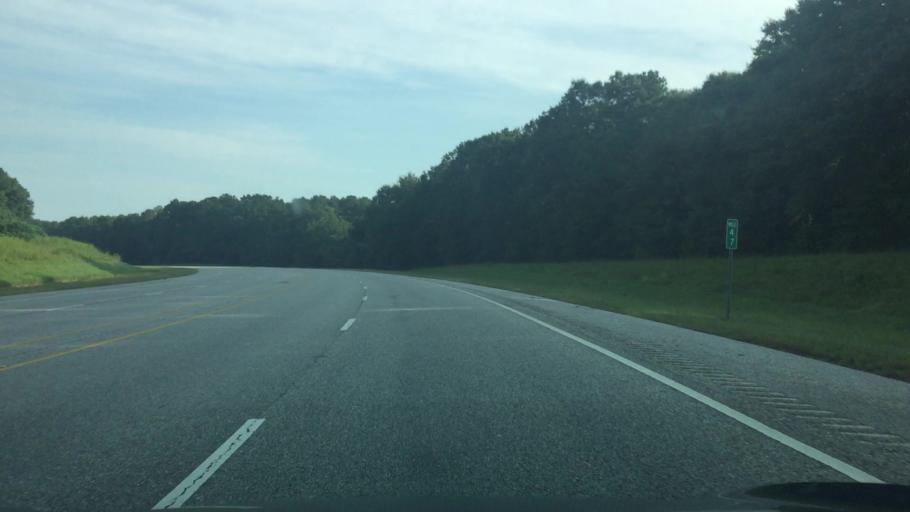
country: US
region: Alabama
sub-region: Butler County
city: Georgiana
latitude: 31.5108
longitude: -86.7014
